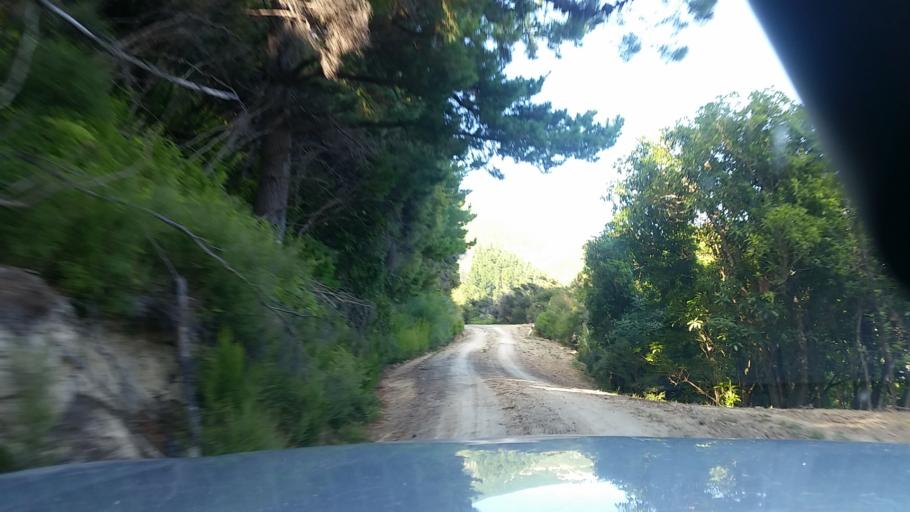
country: NZ
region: Marlborough
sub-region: Marlborough District
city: Picton
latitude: -41.3110
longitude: 174.1716
